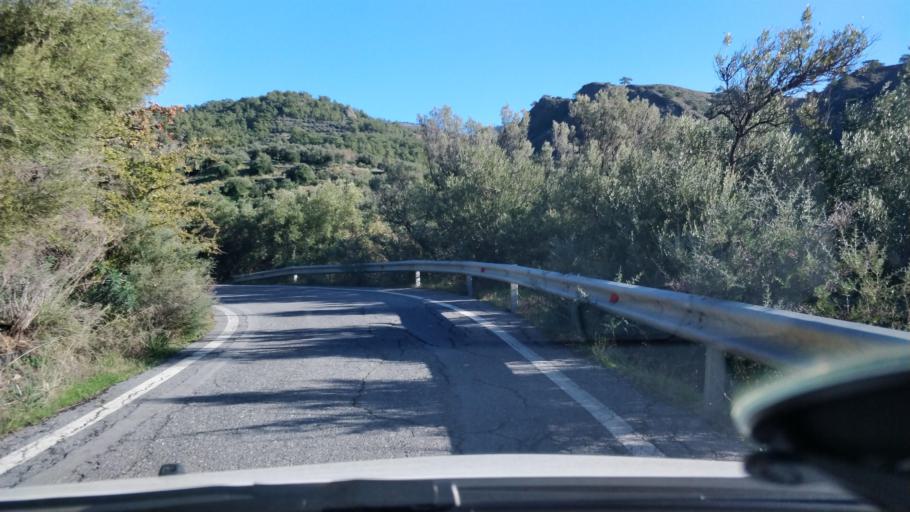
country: GR
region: Crete
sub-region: Nomos Lasithiou
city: Gra Liyia
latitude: 35.0497
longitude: 25.5793
